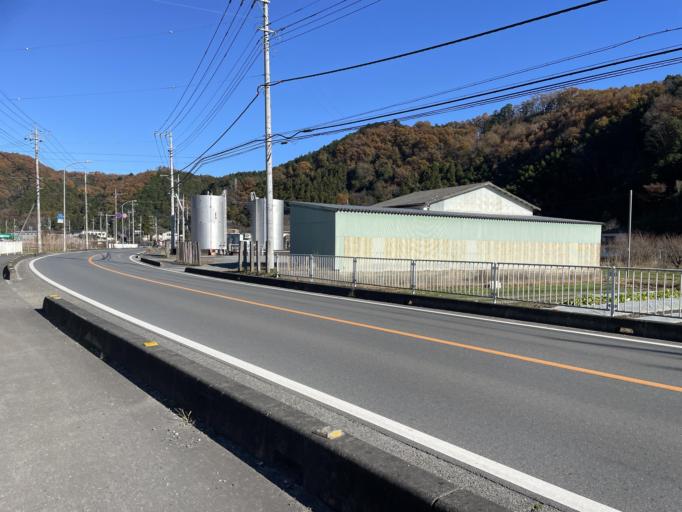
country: JP
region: Saitama
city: Ogawa
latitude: 36.0430
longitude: 139.2284
